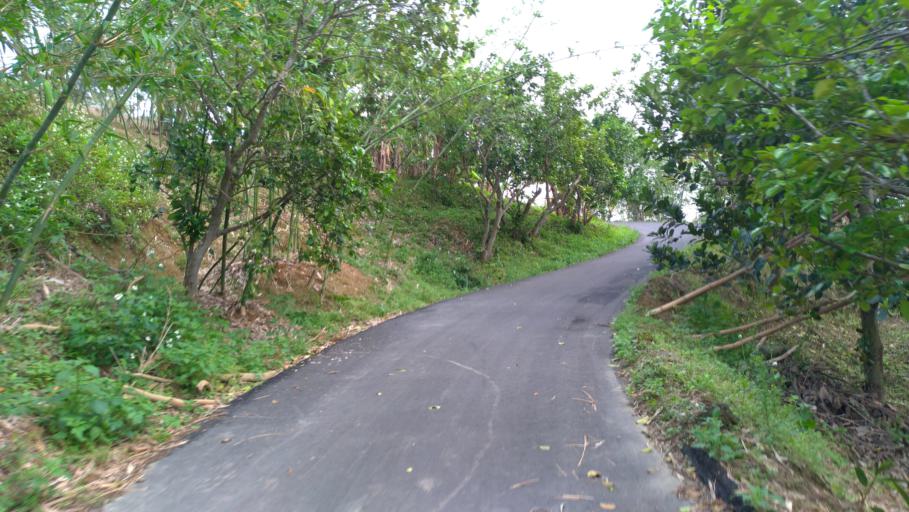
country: TW
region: Taiwan
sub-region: Hsinchu
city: Hsinchu
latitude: 24.7562
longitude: 120.9777
